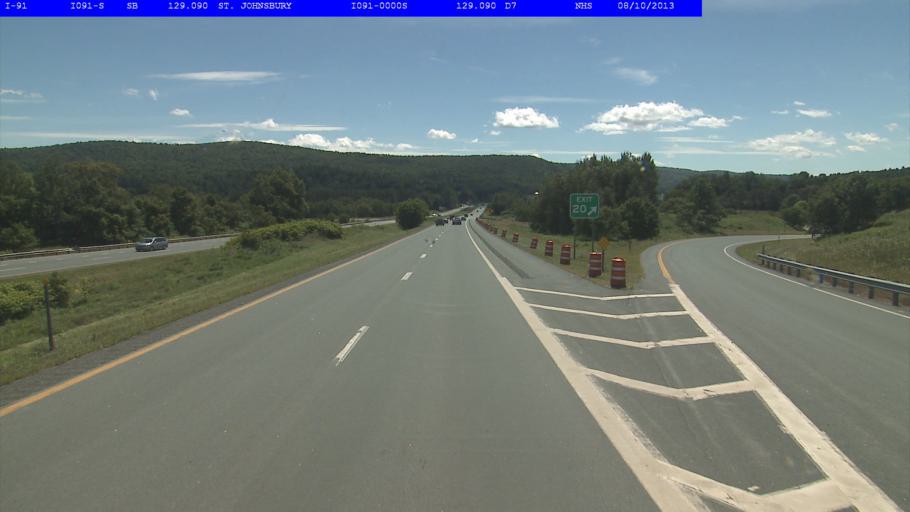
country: US
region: Vermont
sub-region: Caledonia County
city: Saint Johnsbury
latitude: 44.4073
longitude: -72.0249
